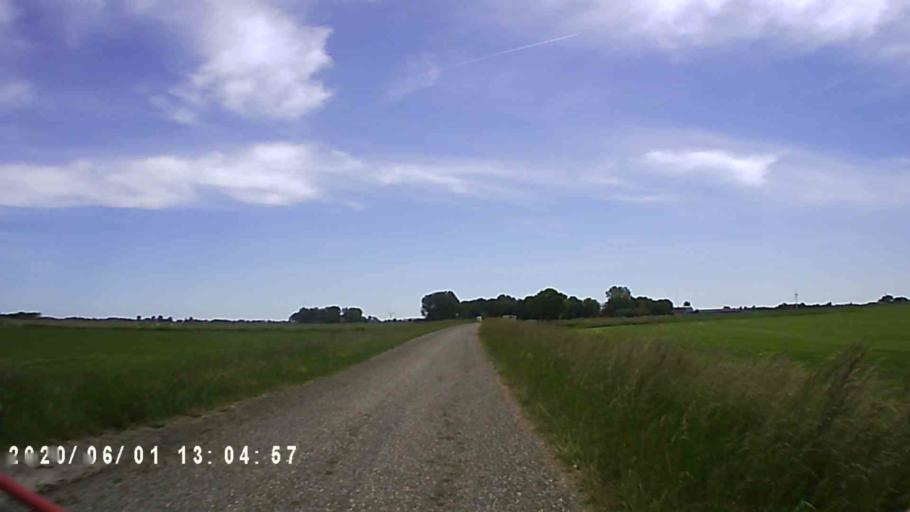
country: NL
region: Friesland
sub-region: Gemeente Franekeradeel
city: Tzum
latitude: 53.1379
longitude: 5.5459
